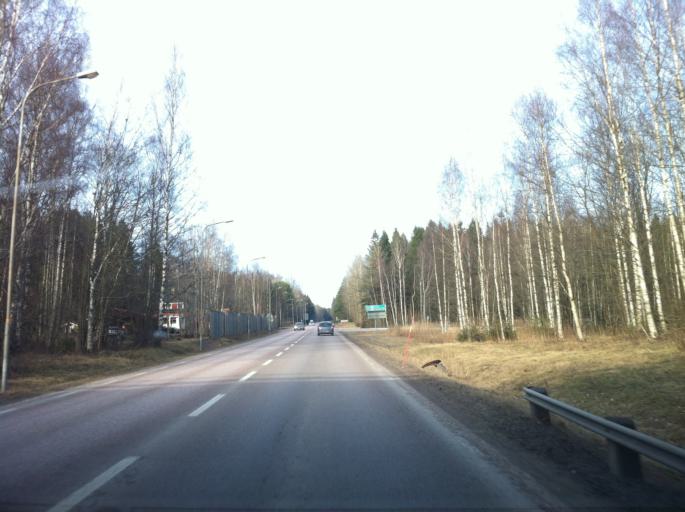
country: SE
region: Vaermland
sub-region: Kristinehamns Kommun
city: Kristinehamn
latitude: 59.3241
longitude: 14.1152
